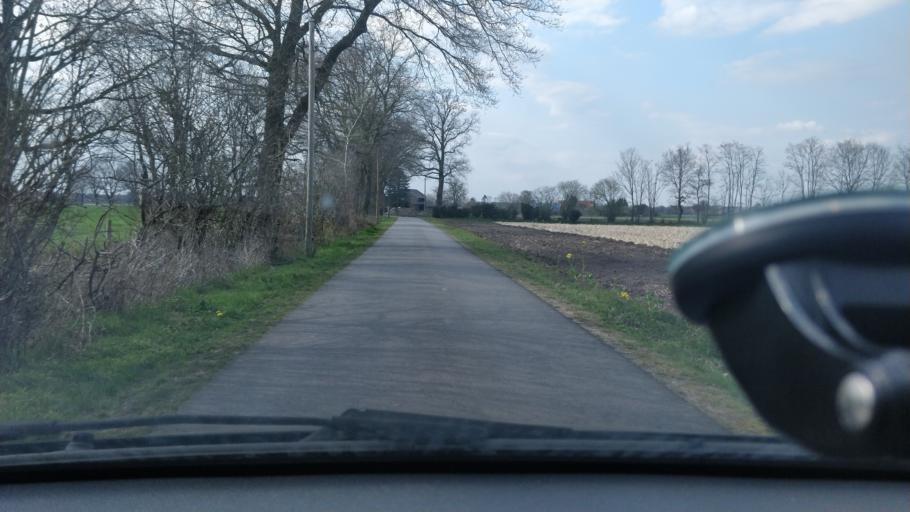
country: DE
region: North Rhine-Westphalia
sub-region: Regierungsbezirk Dusseldorf
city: Bocholt
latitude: 51.8882
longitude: 6.6328
